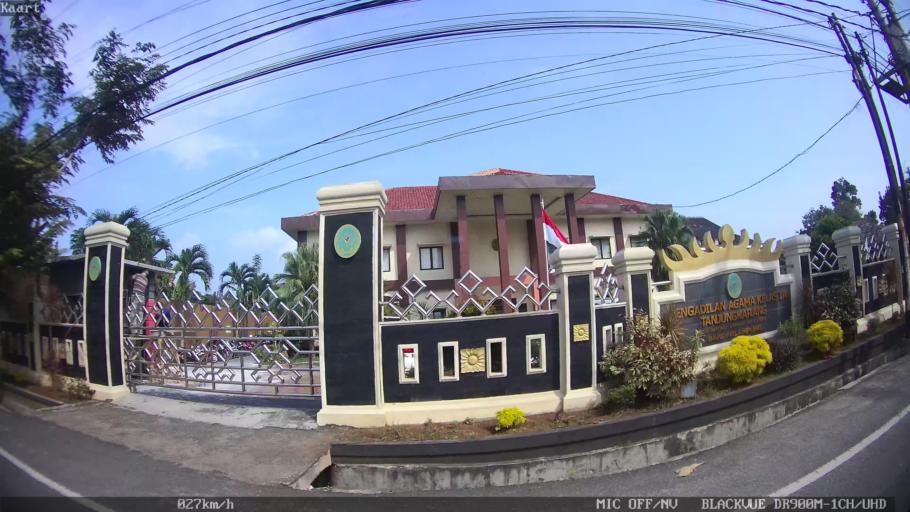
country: ID
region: Lampung
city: Kedaton
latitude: -5.3754
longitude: 105.2502
